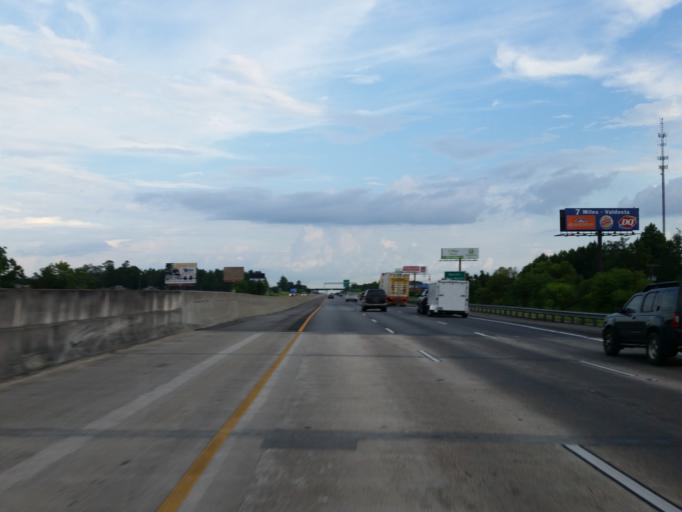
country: US
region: Georgia
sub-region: Lowndes County
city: Hahira
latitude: 31.0005
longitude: -83.3906
